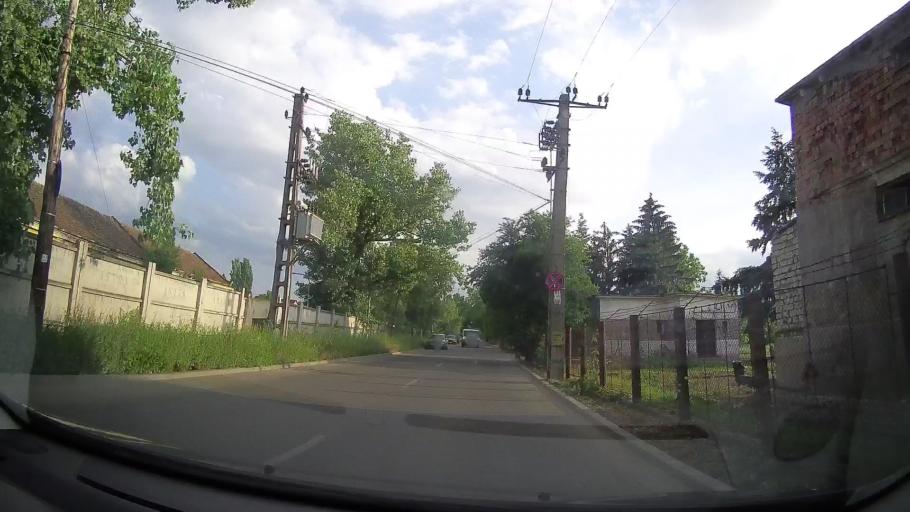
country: RO
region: Timis
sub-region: Comuna Dumbravita
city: Dumbravita
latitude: 45.7804
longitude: 21.2288
